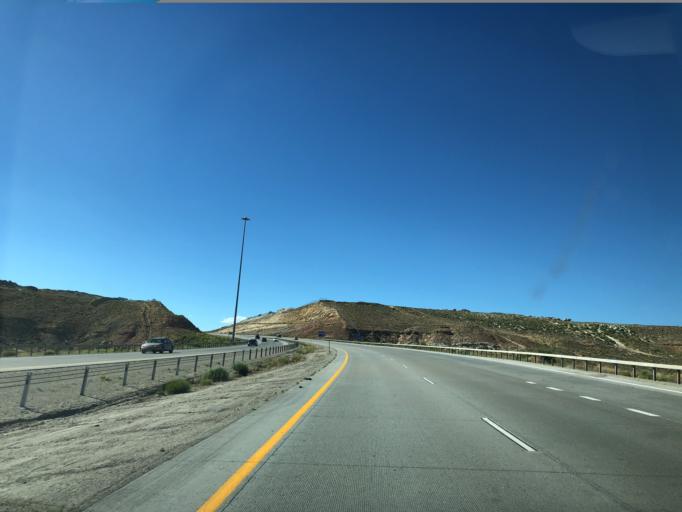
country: US
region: Wyoming
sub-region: Sweetwater County
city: Rock Springs
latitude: 41.5999
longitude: -109.2009
